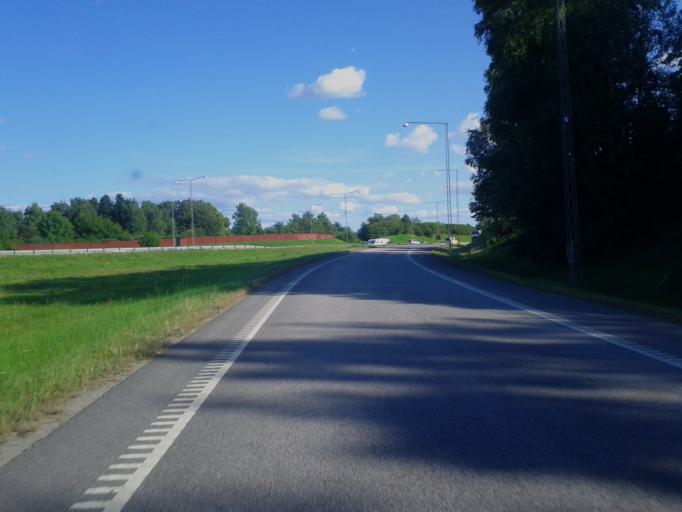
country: SE
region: Stockholm
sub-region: Upplands Vasby Kommun
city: Upplands Vaesby
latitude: 59.4682
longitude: 17.9102
